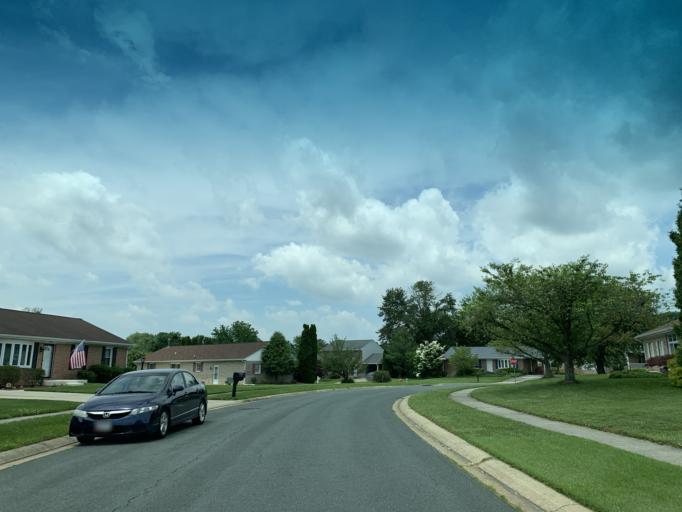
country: US
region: Maryland
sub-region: Harford County
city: Bel Air South
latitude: 39.5393
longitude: -76.2963
